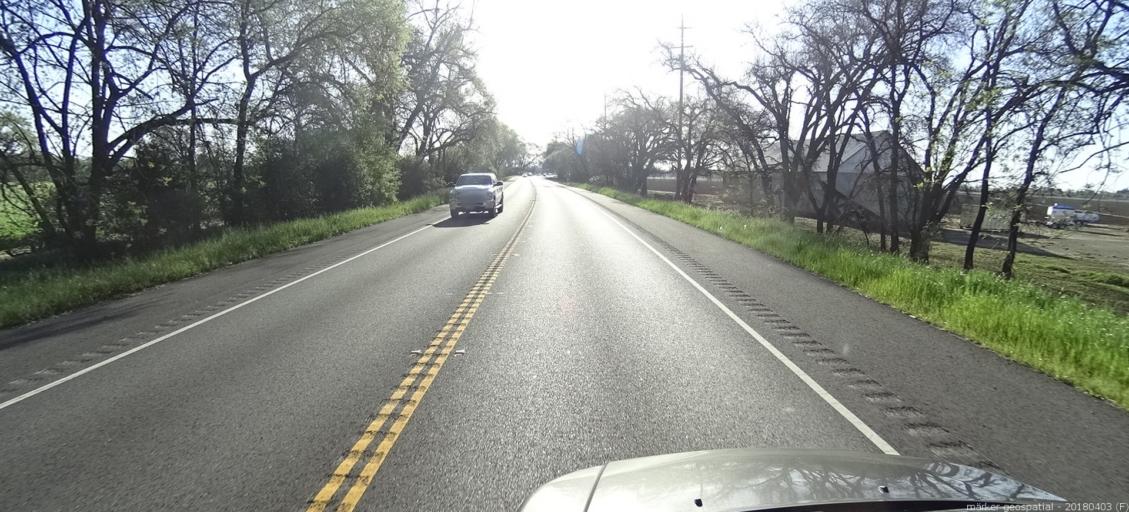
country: US
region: California
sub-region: Sacramento County
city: Rancho Murieta
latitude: 38.4954
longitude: -121.1899
